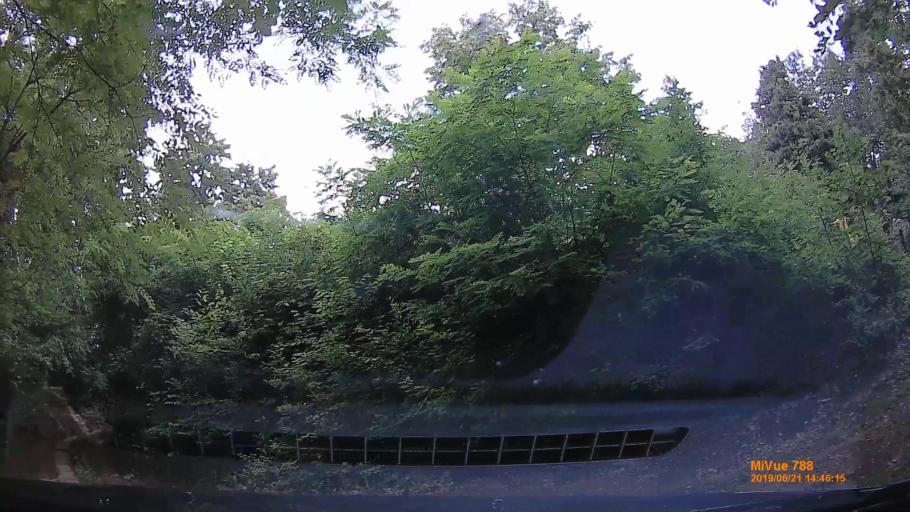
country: HU
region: Baranya
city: Hosszuheteny
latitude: 46.1298
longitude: 18.3099
